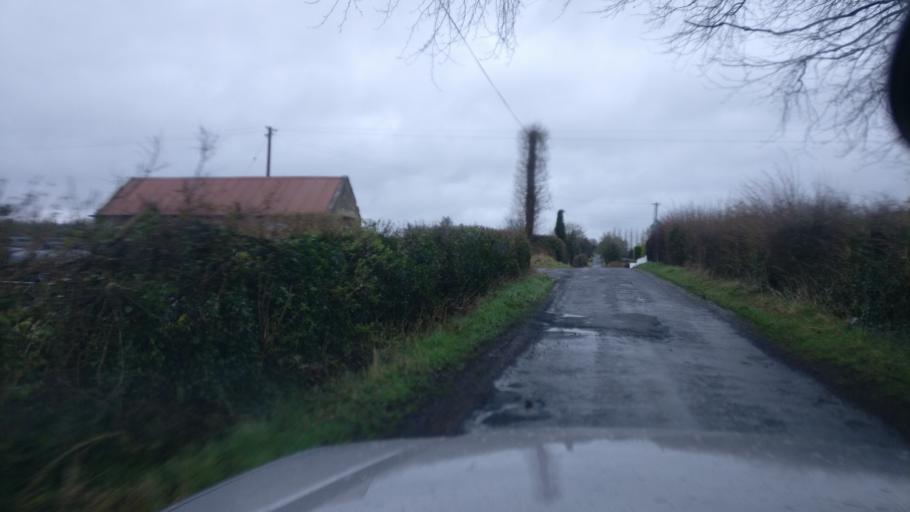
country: IE
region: Connaught
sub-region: County Galway
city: Ballinasloe
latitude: 53.2487
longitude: -8.3572
